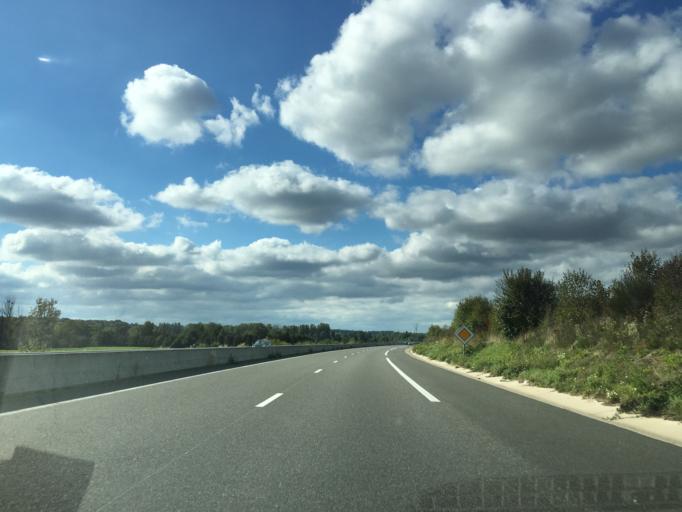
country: FR
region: Lorraine
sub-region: Departement de Meurthe-et-Moselle
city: Gerbeviller
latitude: 48.5253
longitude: 6.6052
